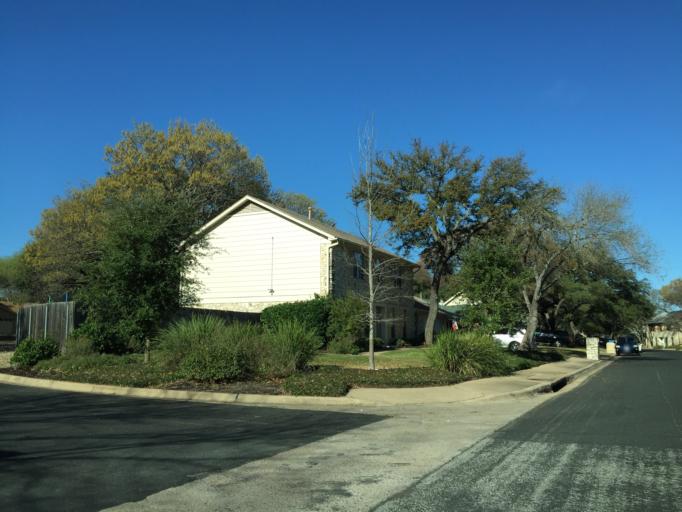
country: US
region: Texas
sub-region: Williamson County
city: Jollyville
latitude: 30.4073
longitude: -97.7346
